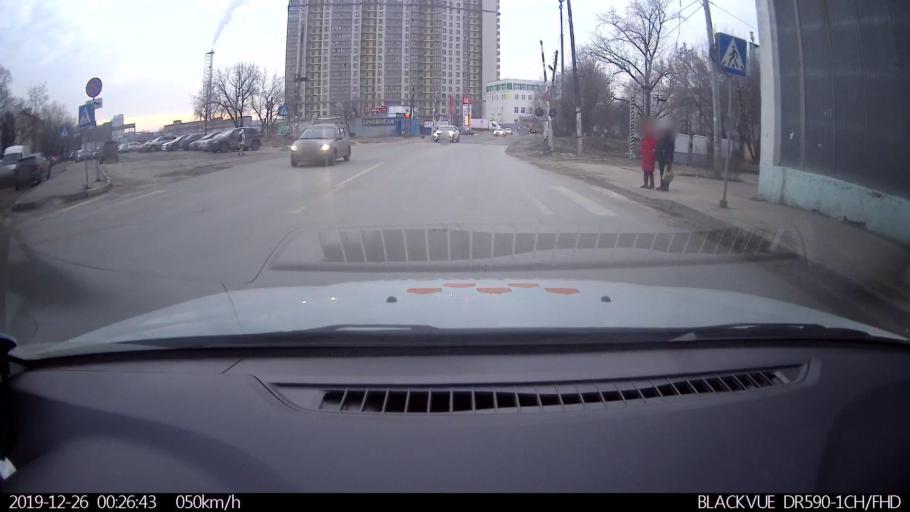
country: RU
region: Nizjnij Novgorod
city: Nizhniy Novgorod
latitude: 56.3104
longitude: 43.9475
